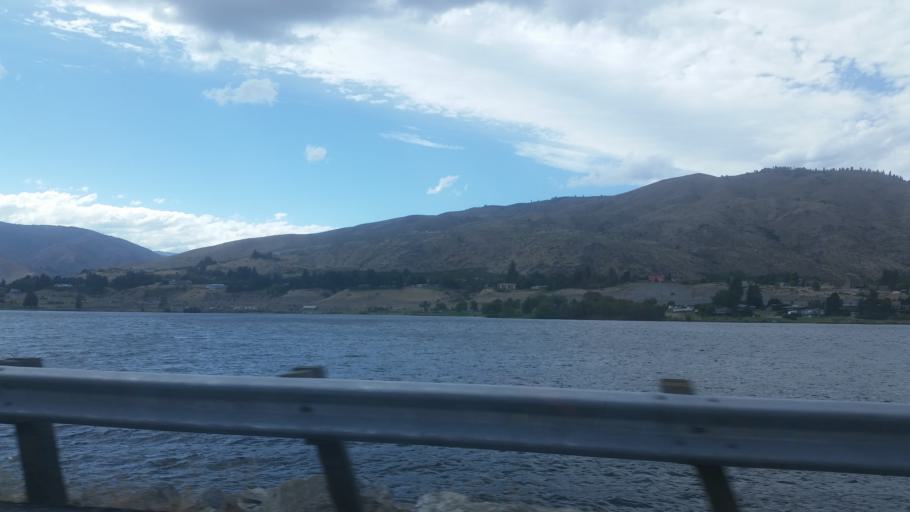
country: US
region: Washington
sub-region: Chelan County
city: Entiat
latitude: 47.6693
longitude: -120.2032
